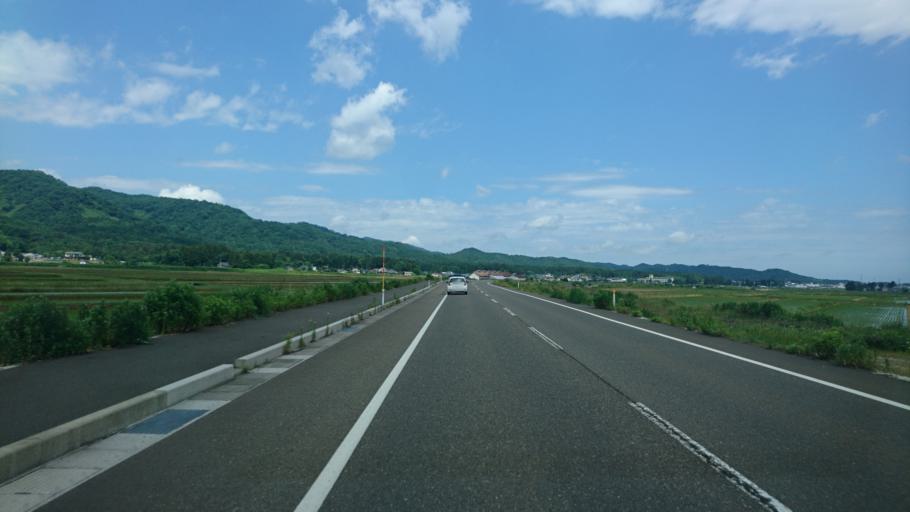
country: JP
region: Niigata
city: Arai
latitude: 37.0716
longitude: 138.2372
